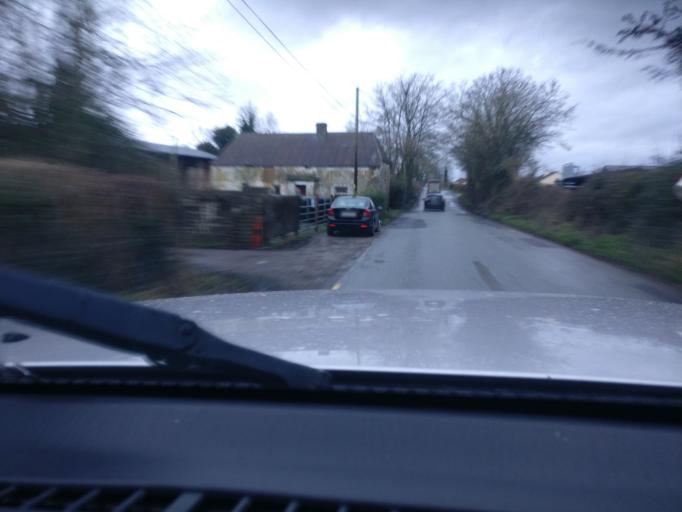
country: IE
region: Leinster
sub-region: An Mhi
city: Longwood
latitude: 53.4469
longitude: -6.9710
